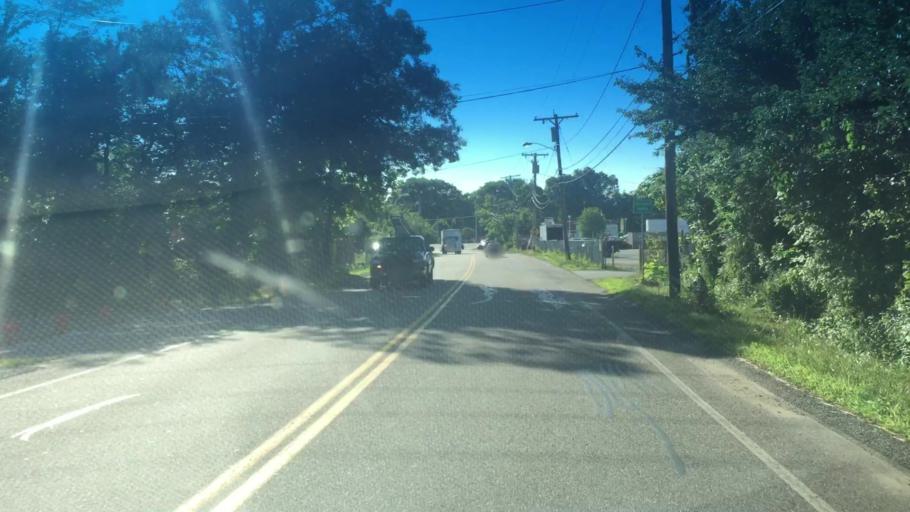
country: US
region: Massachusetts
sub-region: Norfolk County
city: Norwood
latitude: 42.1596
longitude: -71.2037
